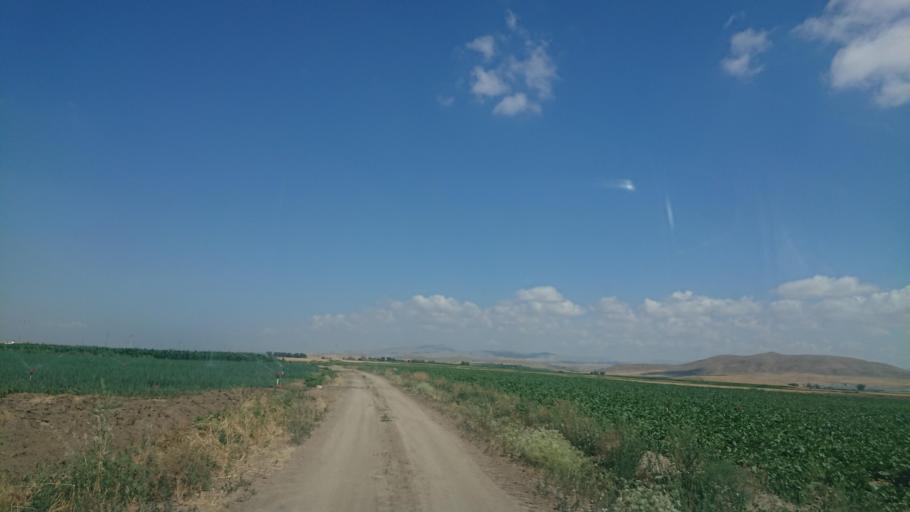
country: TR
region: Aksaray
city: Sariyahsi
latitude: 38.9838
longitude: 33.9066
